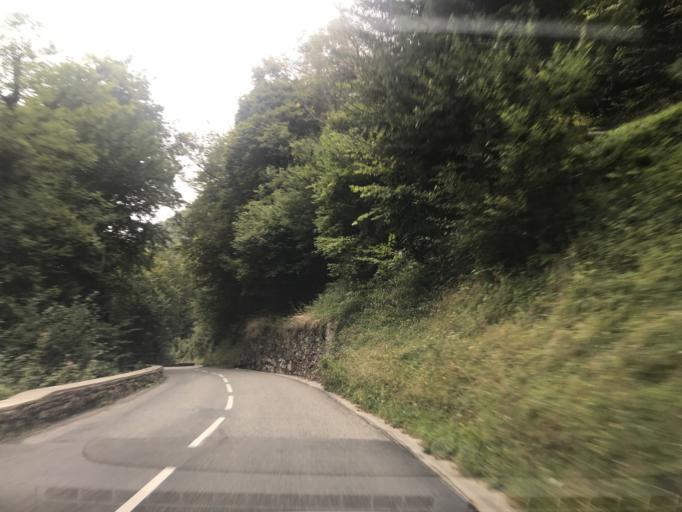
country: FR
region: Midi-Pyrenees
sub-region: Departement de la Haute-Garonne
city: Bagneres-de-Luchon
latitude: 42.7704
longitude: 0.6521
